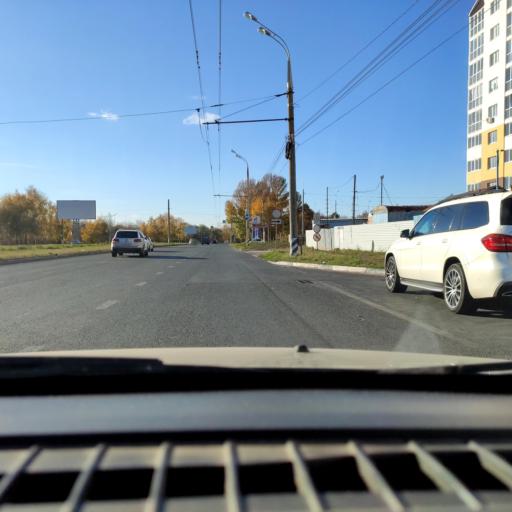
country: RU
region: Samara
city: Tol'yatti
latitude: 53.5001
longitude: 49.2708
